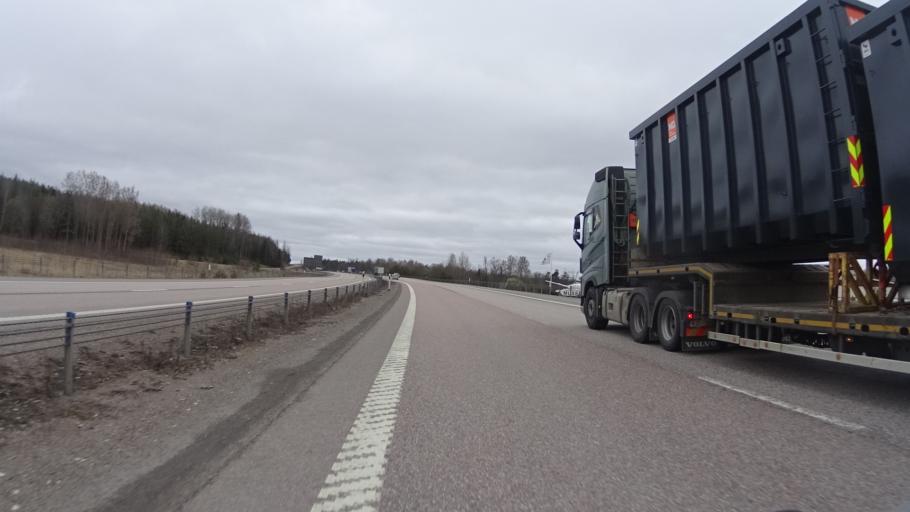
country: SE
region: Soedermanland
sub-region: Strangnas Kommun
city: Strangnas
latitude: 59.3674
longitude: 16.9353
